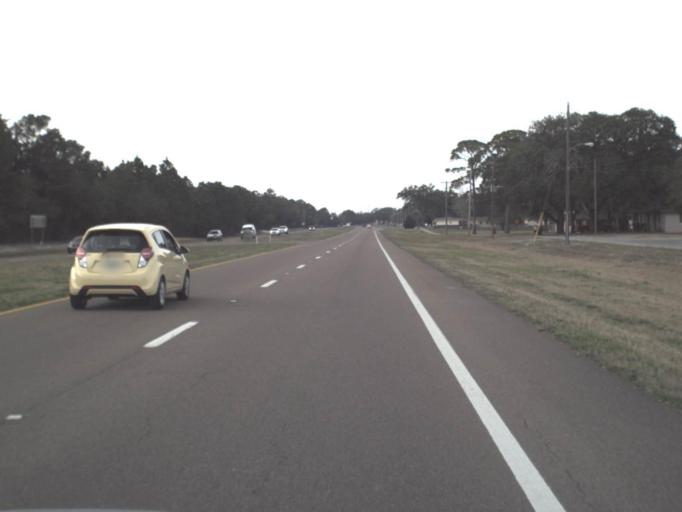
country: US
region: Florida
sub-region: Bay County
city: Tyndall Air Force Base
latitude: 30.0903
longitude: -85.6106
